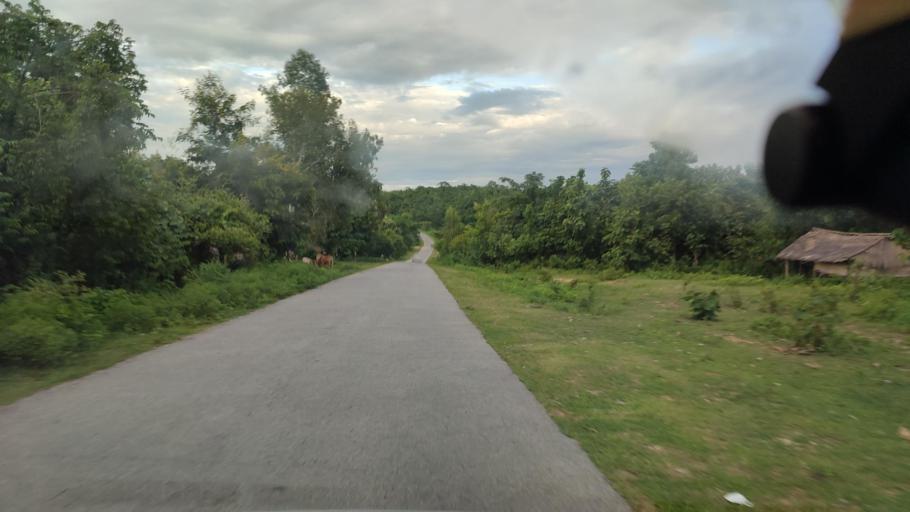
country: MM
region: Mandalay
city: Nay Pyi Taw
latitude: 19.9949
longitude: 95.9331
